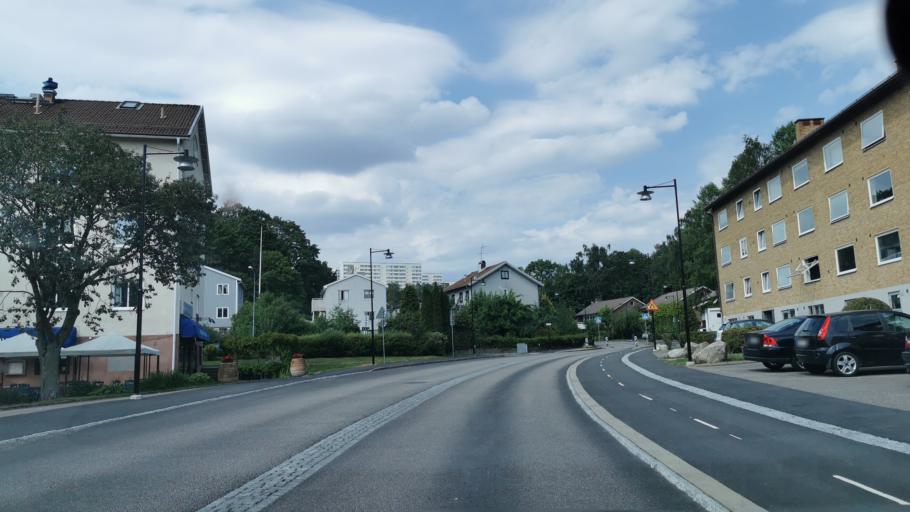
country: SE
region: Vaestra Goetaland
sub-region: Molndal
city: Moelndal
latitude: 57.6767
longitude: 11.9901
